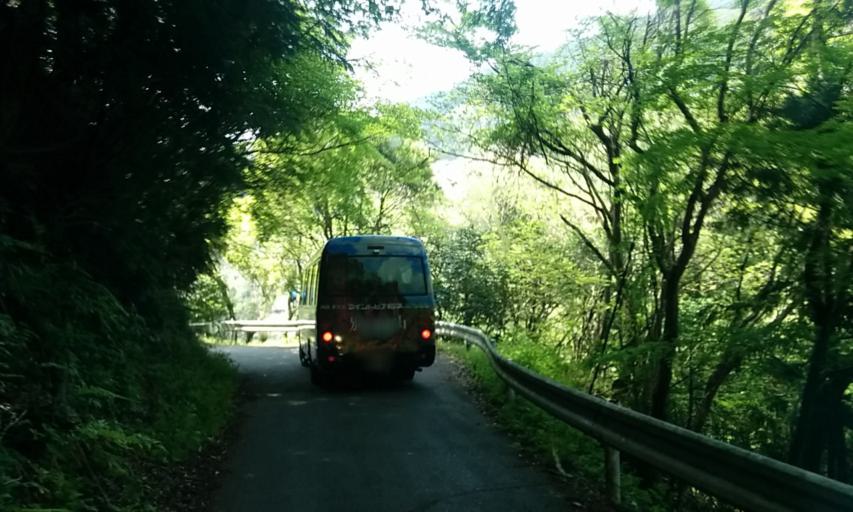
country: JP
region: Ehime
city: Niihama
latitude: 33.8693
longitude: 133.2940
